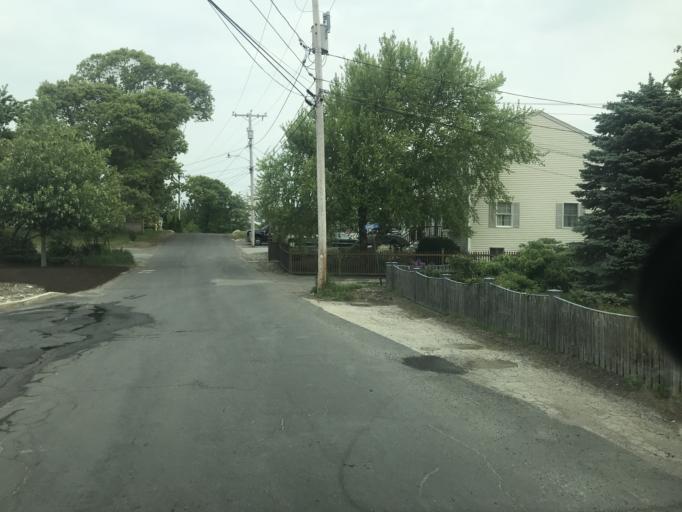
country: US
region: Massachusetts
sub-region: Essex County
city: Rockport
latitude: 42.6454
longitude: -70.6315
